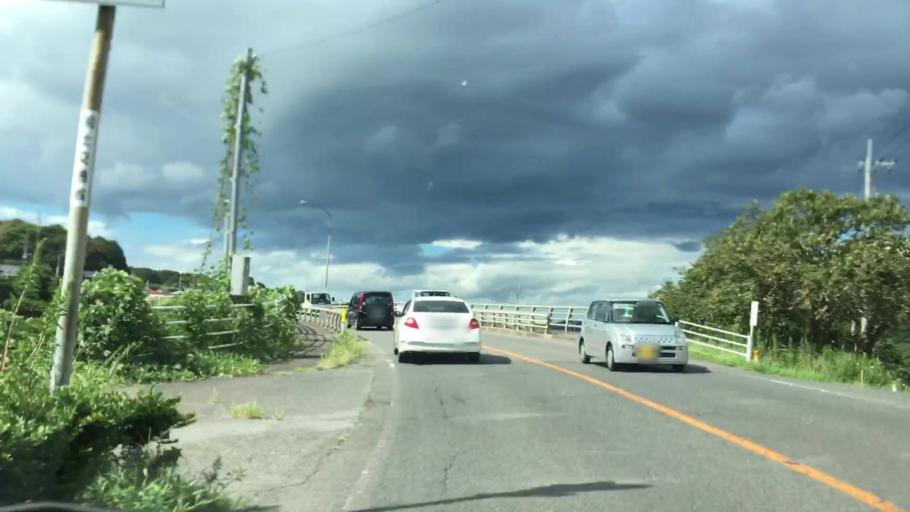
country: JP
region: Saga Prefecture
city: Imaricho-ko
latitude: 33.2405
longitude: 129.8508
